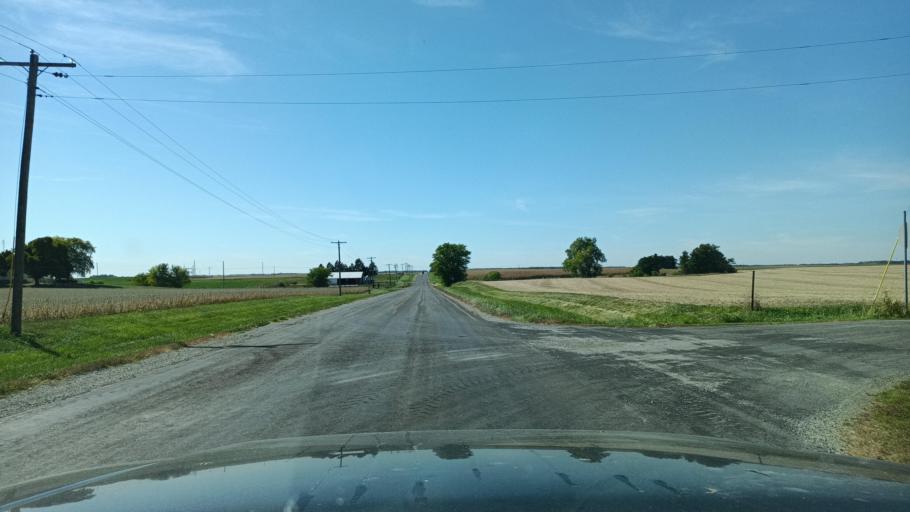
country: US
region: Illinois
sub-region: De Witt County
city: Farmer City
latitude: 40.2240
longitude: -88.7367
